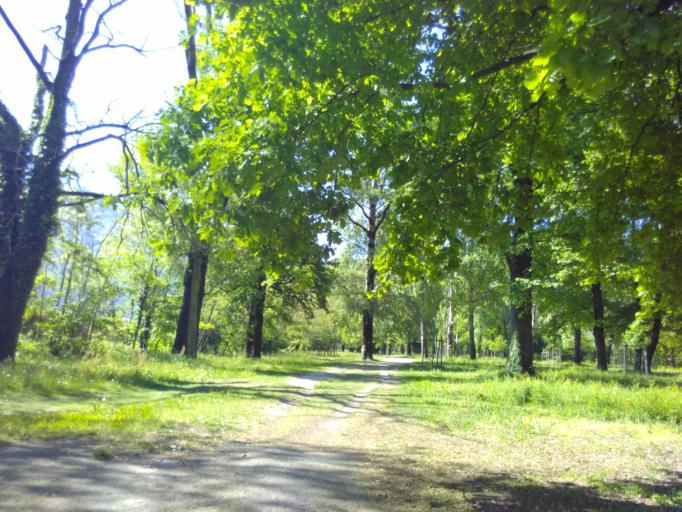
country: CH
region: Ticino
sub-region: Bellinzona District
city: Bellinzona
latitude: 46.1899
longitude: 9.0083
